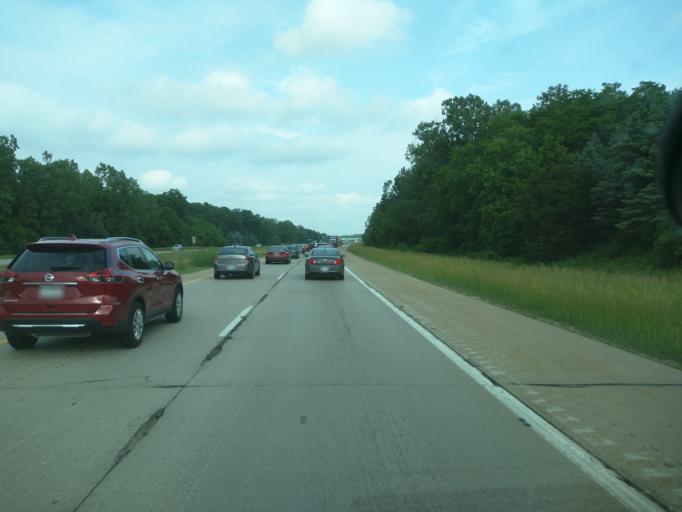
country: US
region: Michigan
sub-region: Clinton County
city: Bath
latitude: 42.8023
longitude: -84.4653
